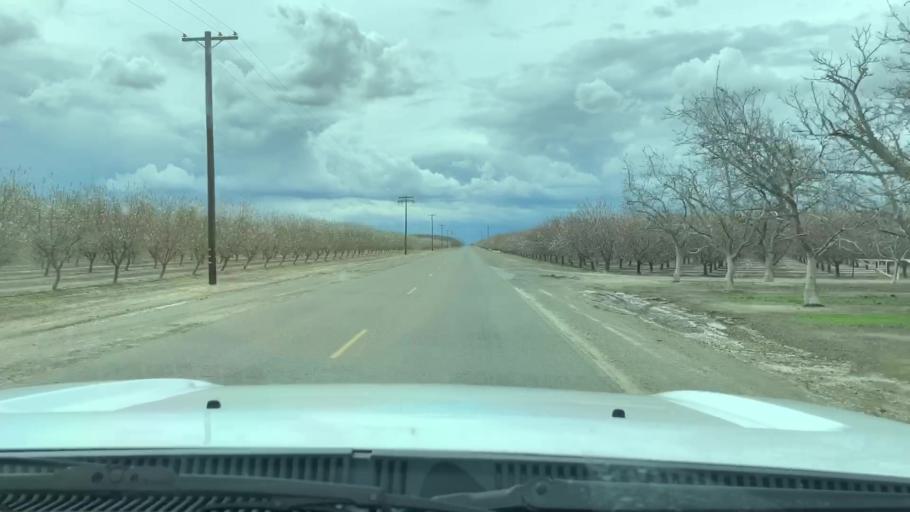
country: US
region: California
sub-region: Fresno County
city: Caruthers
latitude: 36.4894
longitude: -119.7639
